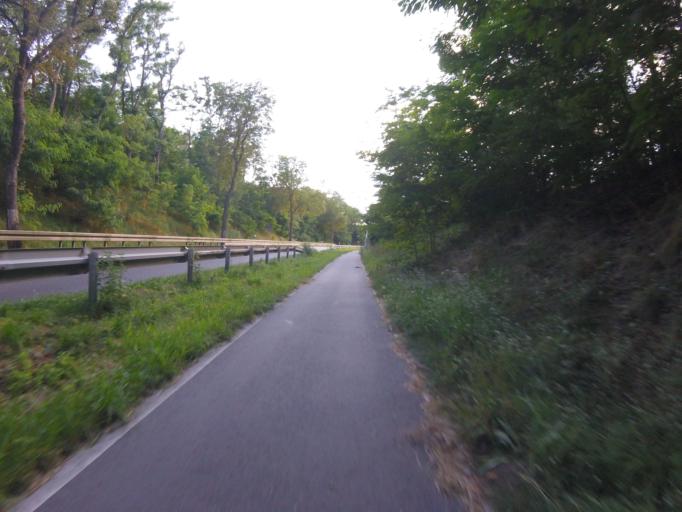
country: DE
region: Brandenburg
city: Zossen
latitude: 52.2190
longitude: 13.4780
